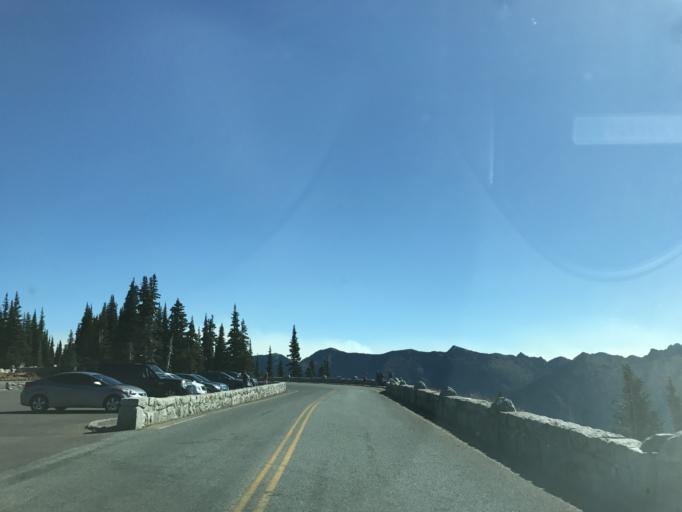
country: US
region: Washington
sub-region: King County
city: Enumclaw
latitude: 46.9171
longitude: -121.5886
